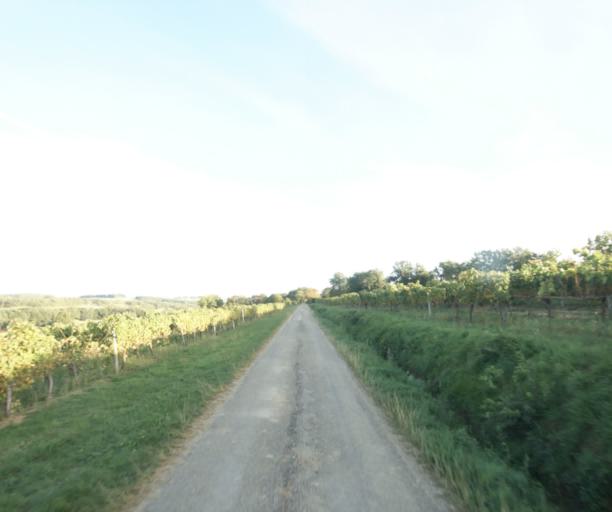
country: FR
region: Midi-Pyrenees
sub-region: Departement du Gers
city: Gondrin
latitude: 43.8750
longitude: 0.2870
